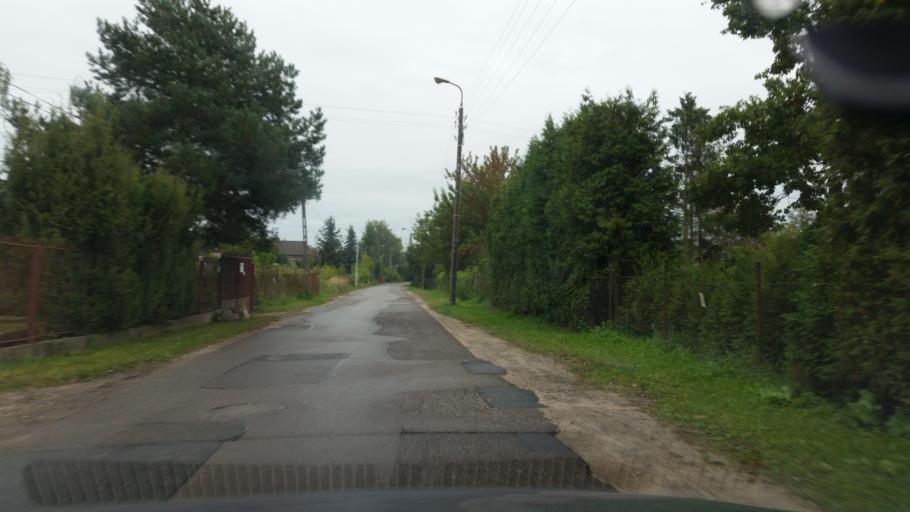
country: PL
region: Masovian Voivodeship
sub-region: Powiat piaseczynski
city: Konstancin-Jeziorna
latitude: 52.0863
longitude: 21.0855
